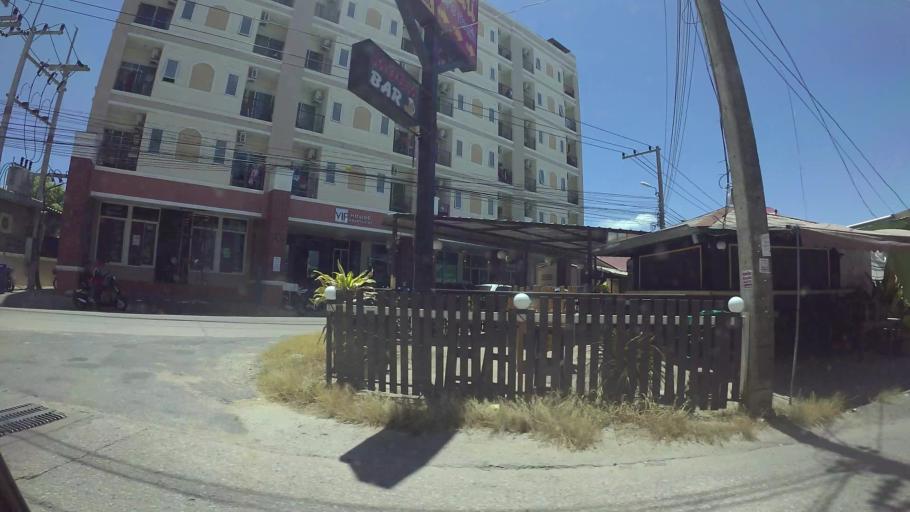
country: TH
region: Chon Buri
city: Phatthaya
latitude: 12.9246
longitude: 100.8913
